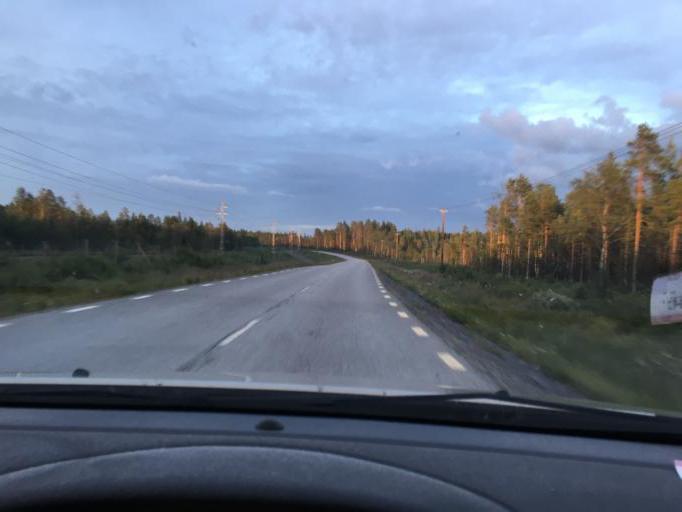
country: SE
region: Norrbotten
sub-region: Lulea Kommun
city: Ranea
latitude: 66.0402
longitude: 22.3200
